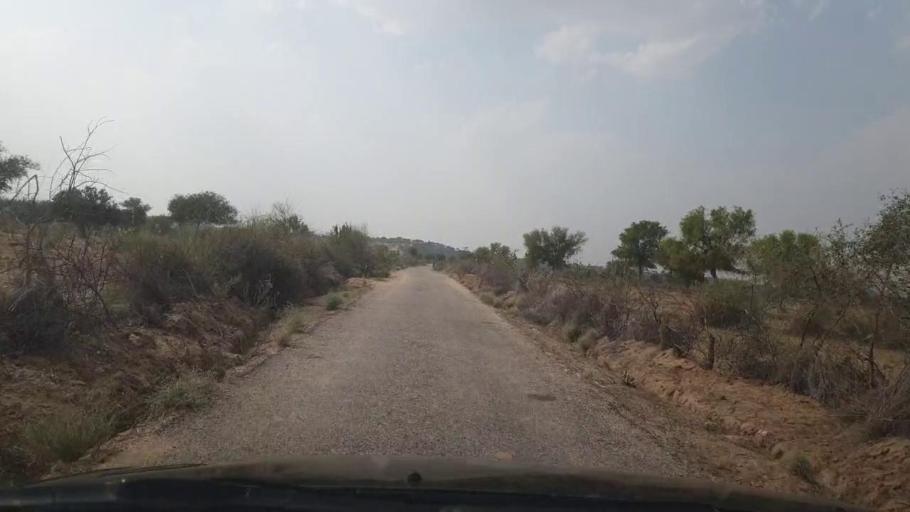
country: PK
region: Sindh
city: Islamkot
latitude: 24.9656
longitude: 70.6220
